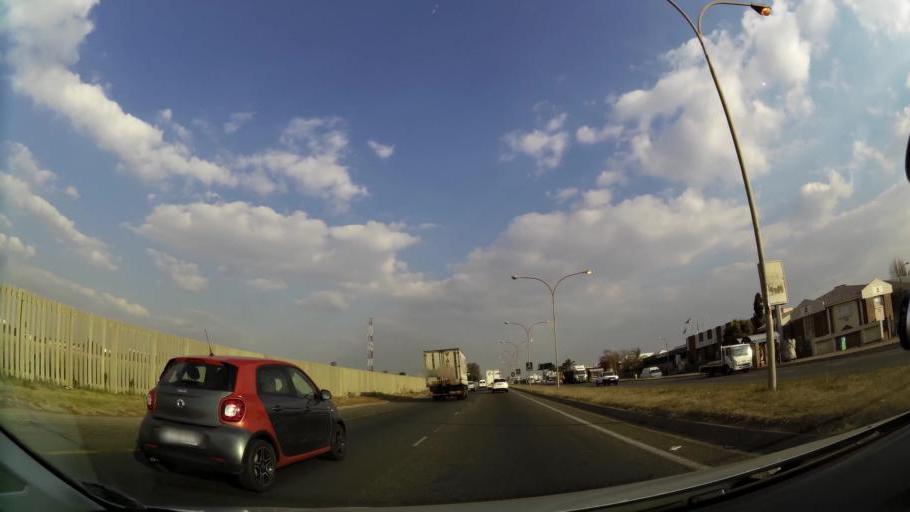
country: ZA
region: Gauteng
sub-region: City of Johannesburg Metropolitan Municipality
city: Modderfontein
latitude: -26.1293
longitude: 28.2020
